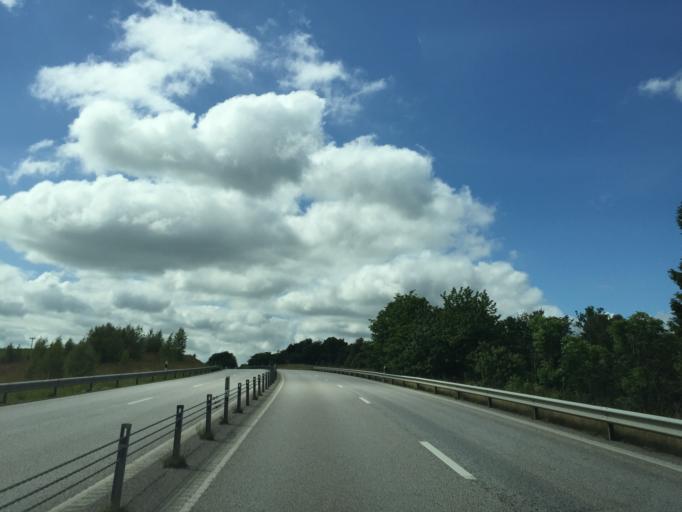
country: SE
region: Skane
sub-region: Trelleborgs Kommun
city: Anderslov
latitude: 55.5003
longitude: 13.4056
